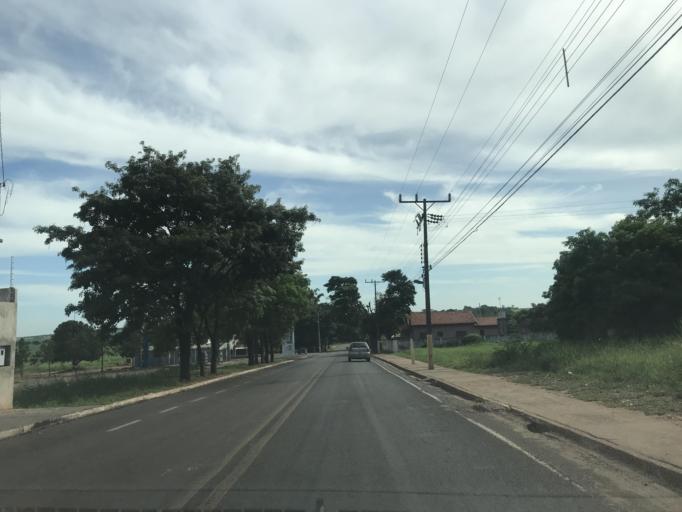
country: BR
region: Parana
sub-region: Paranavai
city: Nova Aurora
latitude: -22.9312
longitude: -52.6839
